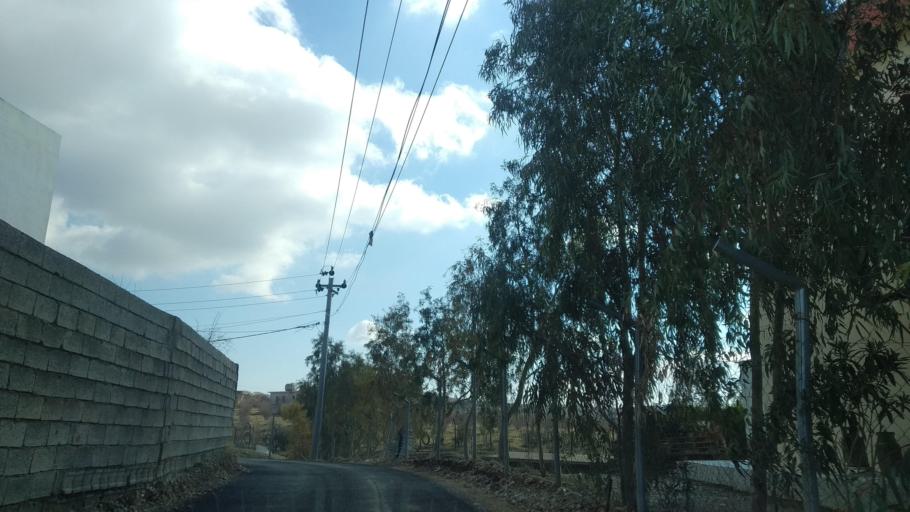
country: IQ
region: Arbil
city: Erbil
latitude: 36.2315
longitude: 44.1539
